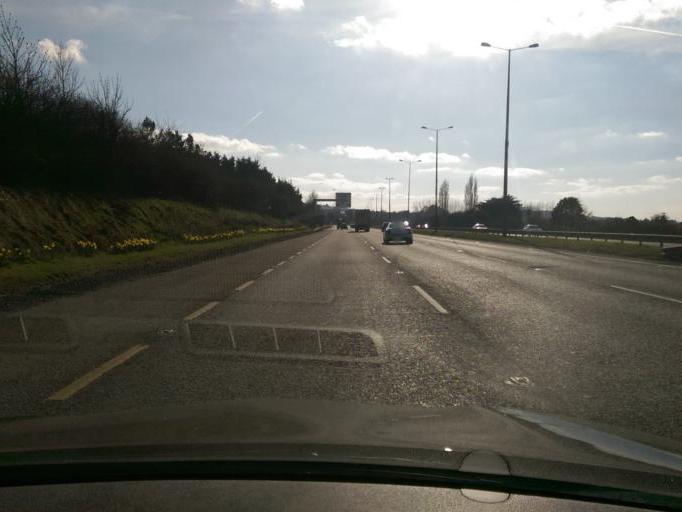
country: IE
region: Leinster
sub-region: South Dublin
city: Saggart
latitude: 53.2884
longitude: -6.4497
